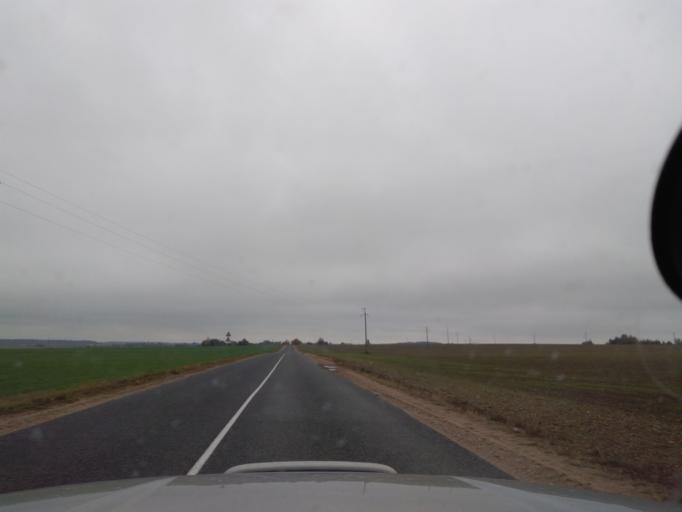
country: BY
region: Minsk
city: Kapyl'
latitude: 53.1542
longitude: 27.1675
